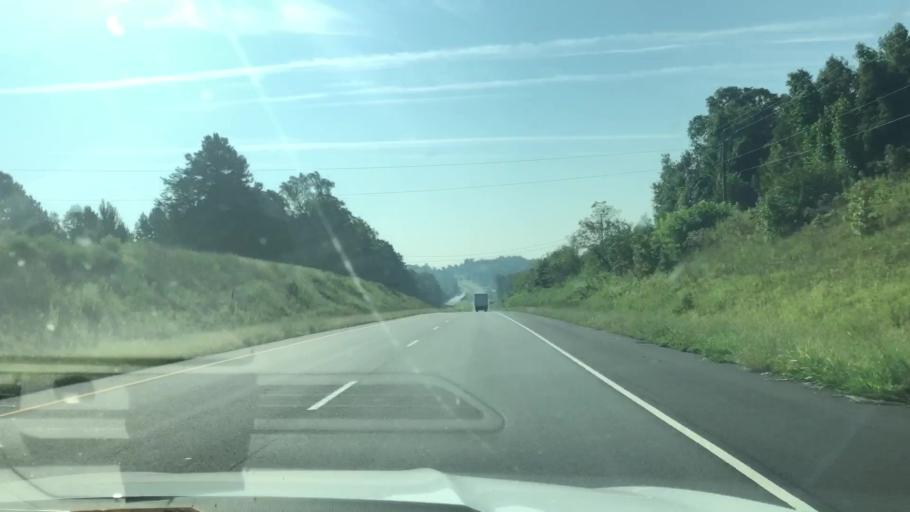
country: US
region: Virginia
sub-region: Richmond County
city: Warsaw
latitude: 37.9295
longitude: -76.7297
